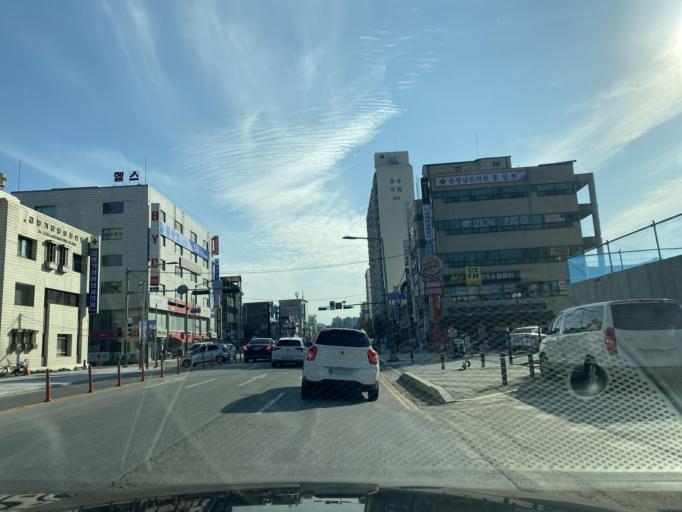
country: KR
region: Chungcheongnam-do
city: Cheonan
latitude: 36.8041
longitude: 127.1588
